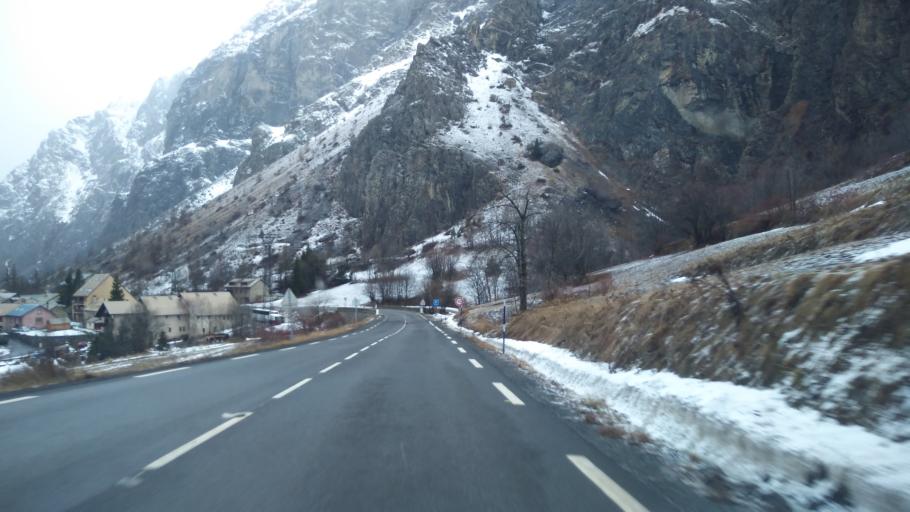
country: FR
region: Rhone-Alpes
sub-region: Departement de l'Isere
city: Mont-de-Lans
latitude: 45.0437
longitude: 6.2868
